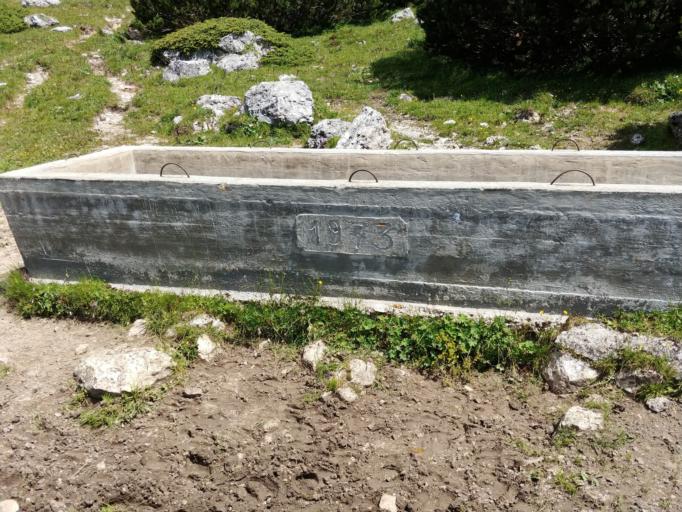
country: IT
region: Trentino-Alto Adige
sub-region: Bolzano
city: Selva
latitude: 46.5940
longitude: 11.7718
